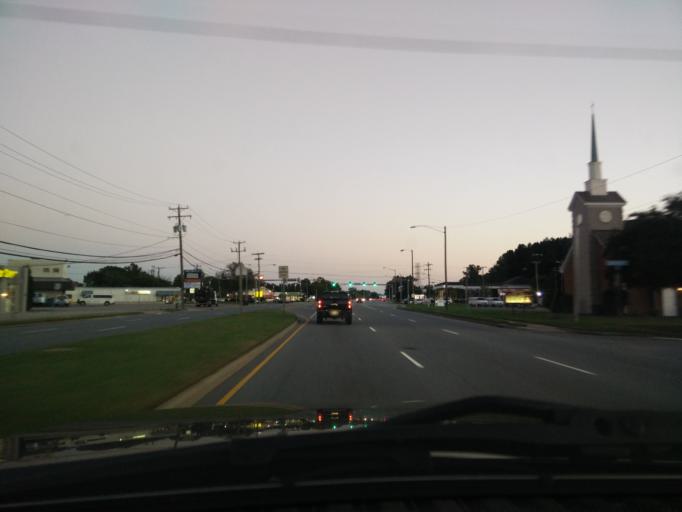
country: US
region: Virginia
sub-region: City of Chesapeake
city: Chesapeake
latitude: 36.7566
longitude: -76.2488
